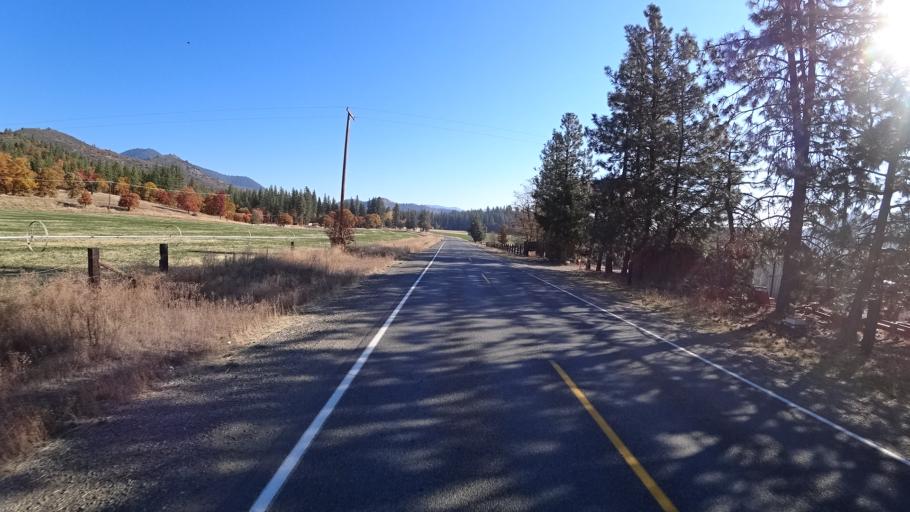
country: US
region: California
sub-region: Siskiyou County
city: Yreka
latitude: 41.6340
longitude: -122.9455
